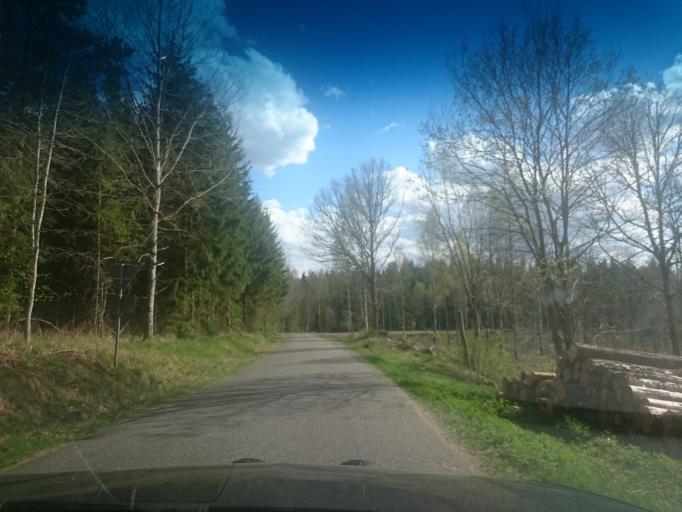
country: SE
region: Kronoberg
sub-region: Vaxjo Kommun
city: Braas
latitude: 57.1479
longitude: 15.1603
